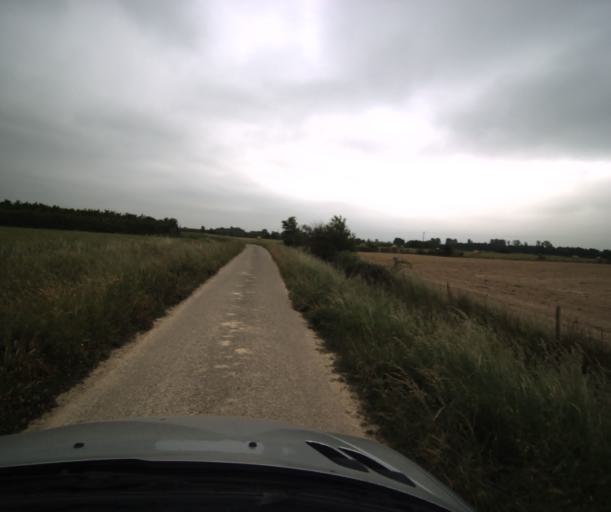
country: FR
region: Midi-Pyrenees
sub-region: Departement du Tarn-et-Garonne
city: Saint-Nicolas-de-la-Grave
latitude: 44.0550
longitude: 0.9774
